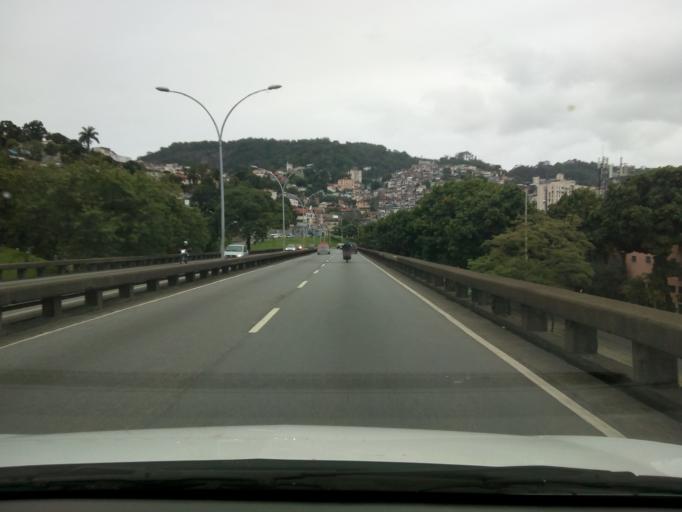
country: BR
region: Rio de Janeiro
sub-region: Rio De Janeiro
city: Rio de Janeiro
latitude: -22.9143
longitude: -43.1949
